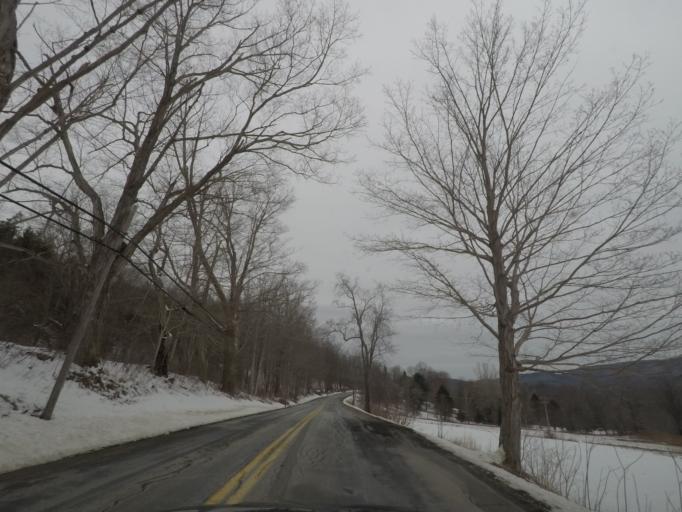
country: US
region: Massachusetts
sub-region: Berkshire County
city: Lanesborough
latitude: 42.5735
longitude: -73.3775
